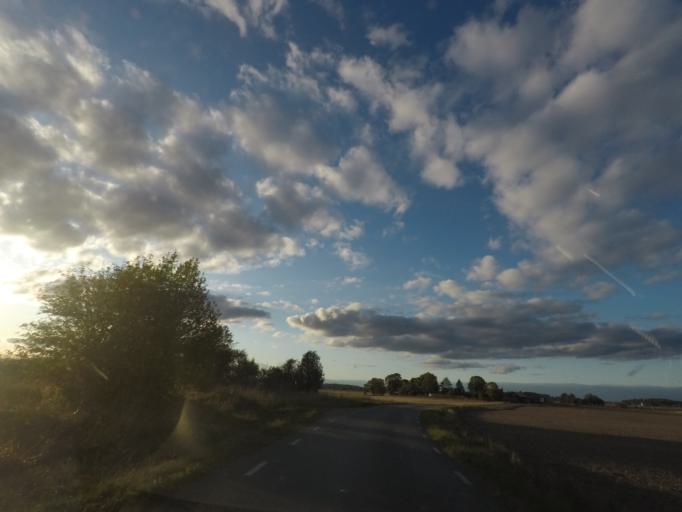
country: SE
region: Vaestmanland
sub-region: Kungsors Kommun
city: Kungsoer
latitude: 59.5246
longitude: 16.1157
